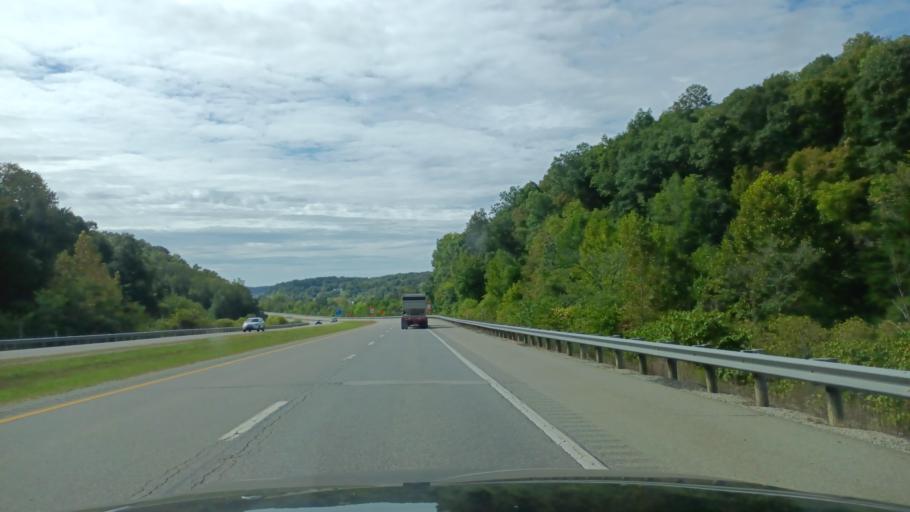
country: US
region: West Virginia
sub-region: Ritchie County
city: Harrisville
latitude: 39.2722
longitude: -81.0365
